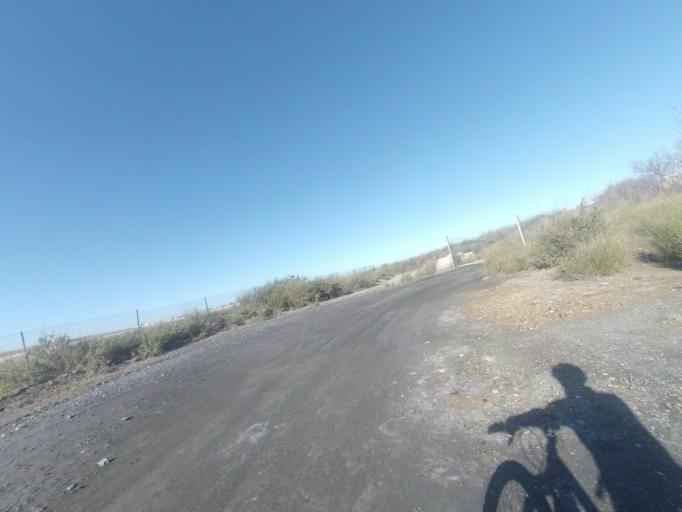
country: ES
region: Andalusia
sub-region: Provincia de Huelva
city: Palos de la Frontera
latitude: 37.2515
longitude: -6.9035
